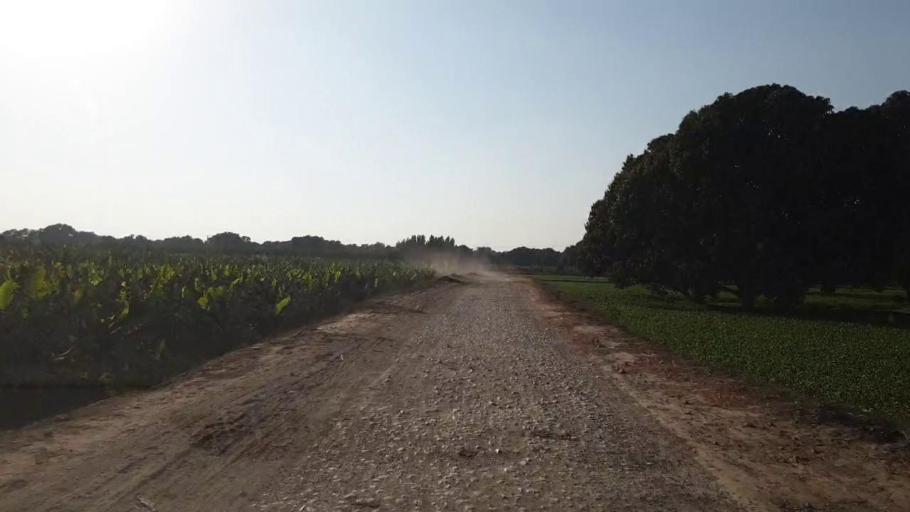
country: PK
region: Sindh
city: Tando Allahyar
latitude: 25.3468
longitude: 68.6598
